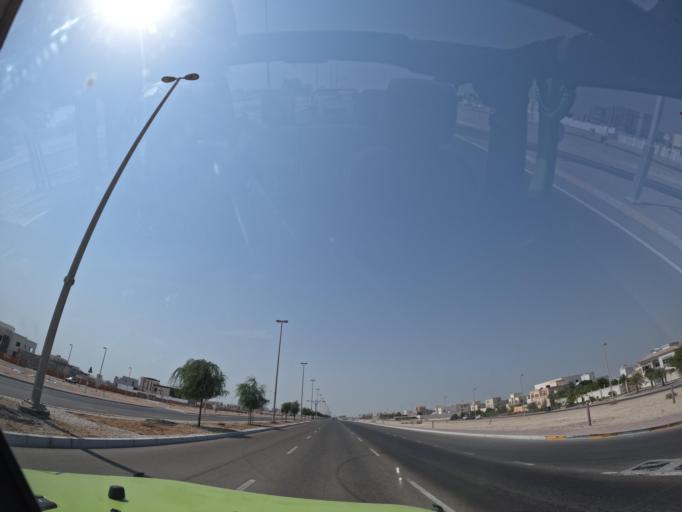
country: AE
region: Abu Dhabi
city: Abu Dhabi
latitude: 24.3513
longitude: 54.6212
